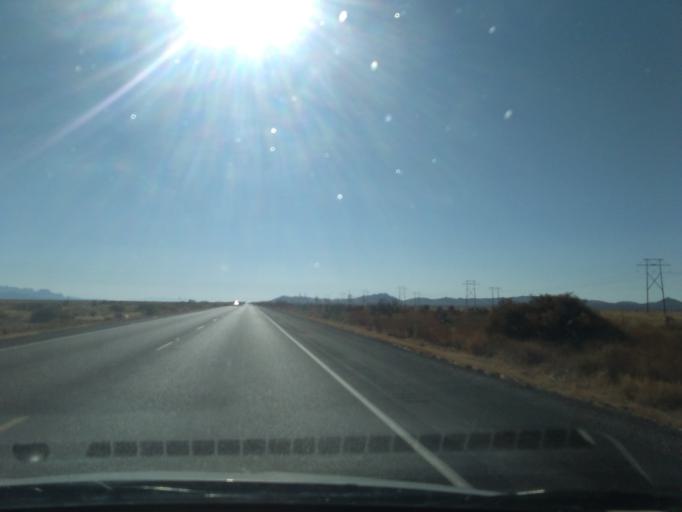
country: US
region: New Mexico
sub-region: Luna County
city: Deming
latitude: 32.4595
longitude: -107.5444
